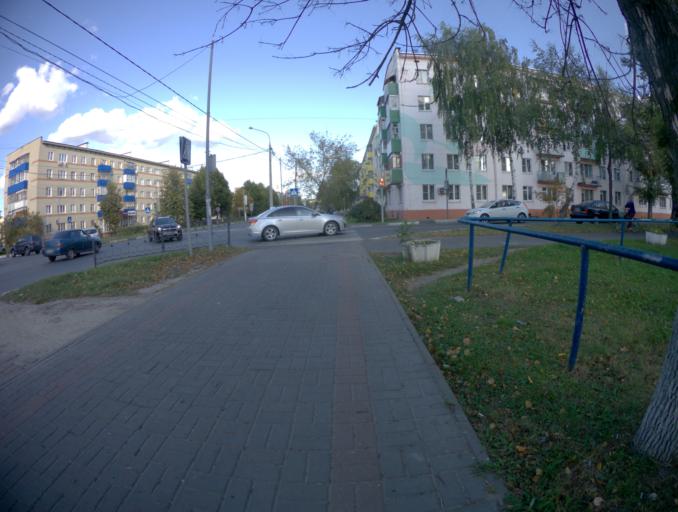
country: RU
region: Moskovskaya
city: Shatura
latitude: 55.5756
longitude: 39.5305
